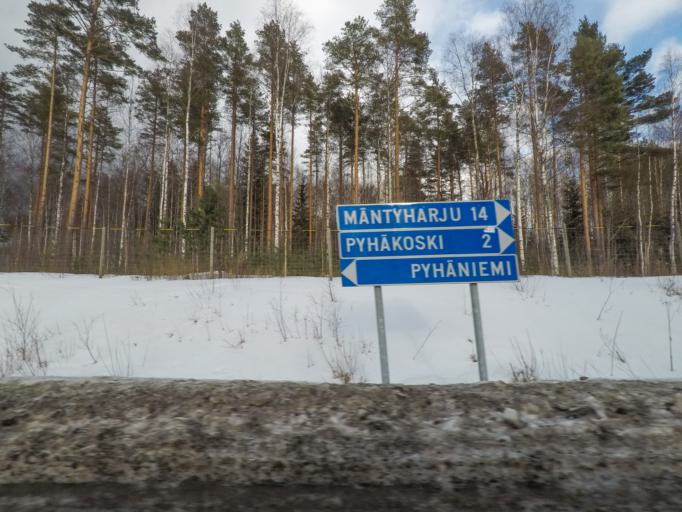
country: FI
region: Southern Savonia
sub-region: Mikkeli
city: Maentyharju
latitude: 61.4422
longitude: 26.6838
